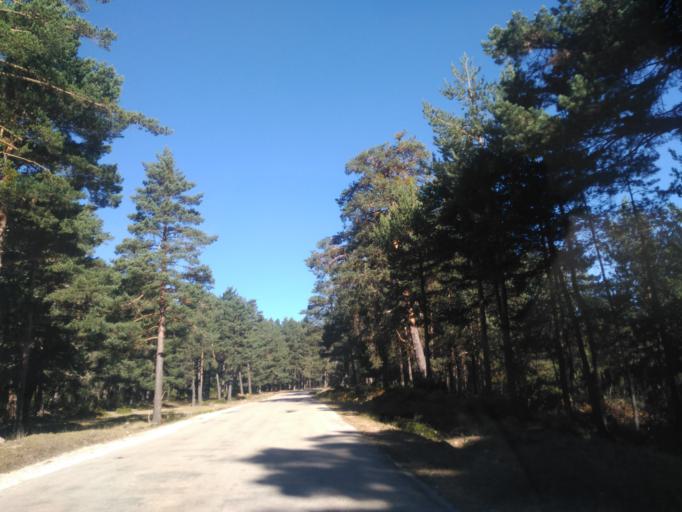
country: ES
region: Castille and Leon
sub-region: Provincia de Soria
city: Vinuesa
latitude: 41.9914
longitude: -2.8001
